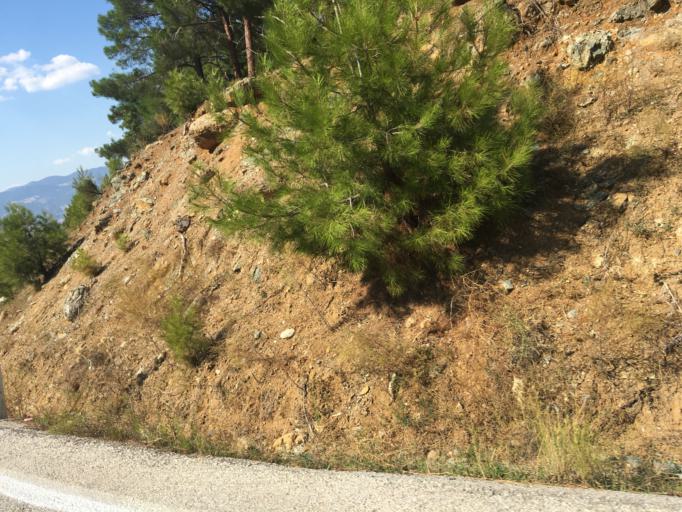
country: TR
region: Ankara
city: Beydili
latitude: 40.0623
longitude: 30.9242
